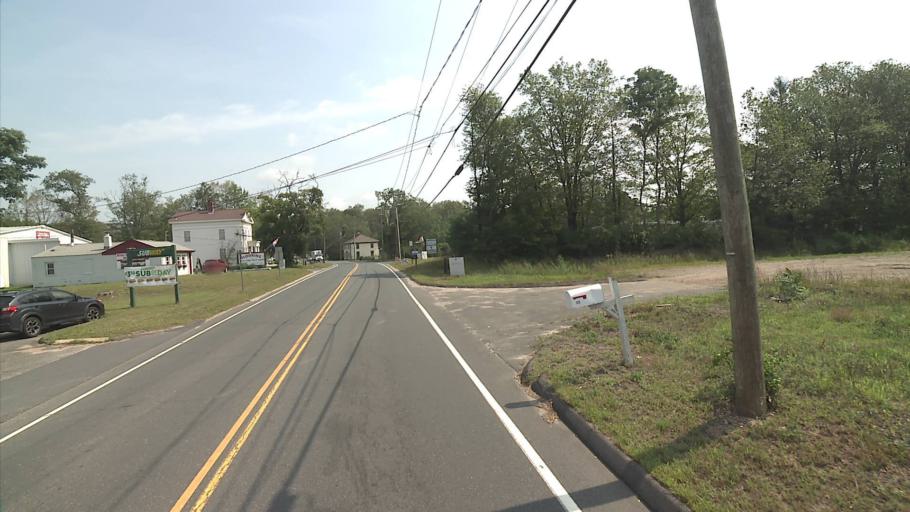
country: US
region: Connecticut
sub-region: Middlesex County
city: East Haddam
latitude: 41.4485
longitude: -72.4741
